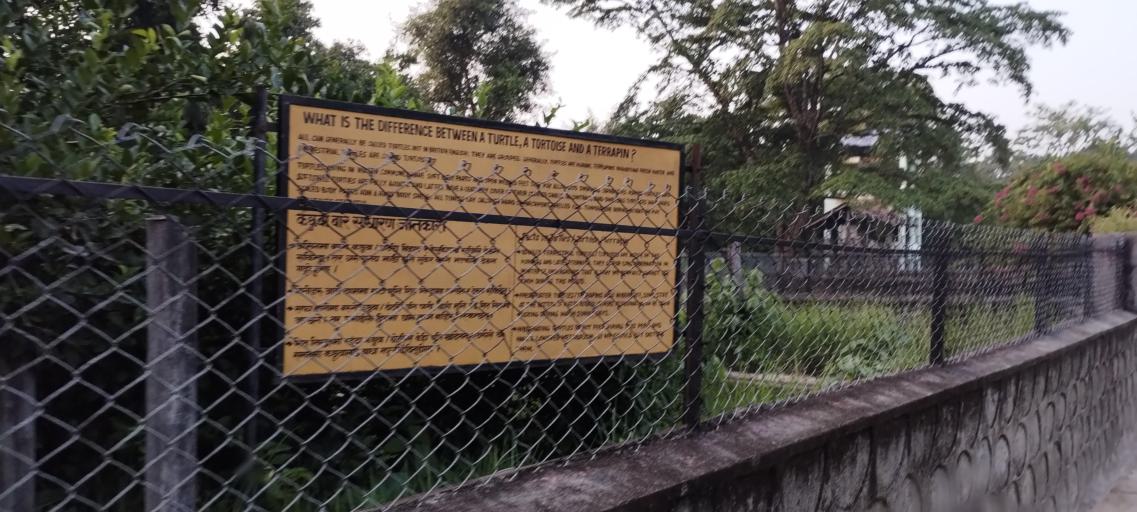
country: NP
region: Far Western
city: Tikapur
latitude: 28.4534
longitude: 81.2414
